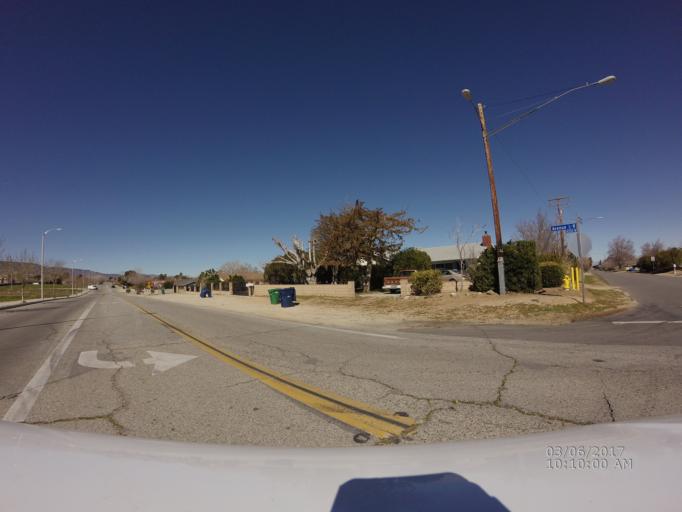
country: US
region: California
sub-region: Los Angeles County
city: Quartz Hill
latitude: 34.6529
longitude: -118.2058
